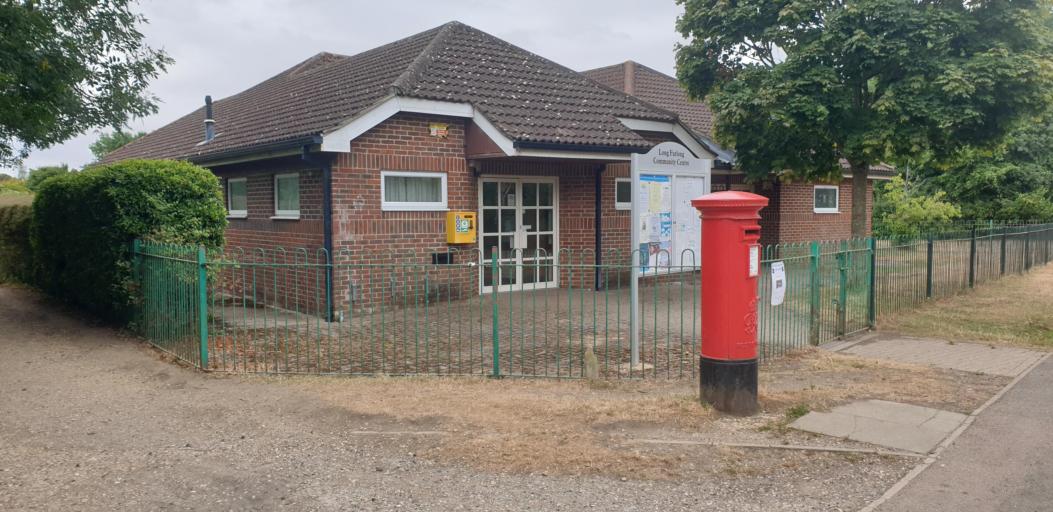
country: GB
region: England
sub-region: Oxfordshire
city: Abingdon
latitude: 51.6883
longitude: -1.2783
